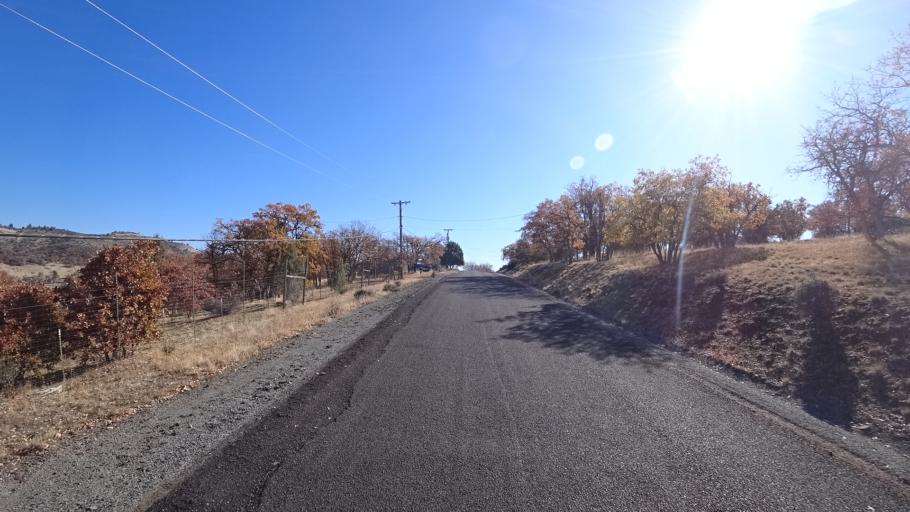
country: US
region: California
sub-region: Siskiyou County
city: Montague
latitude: 41.8802
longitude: -122.4837
